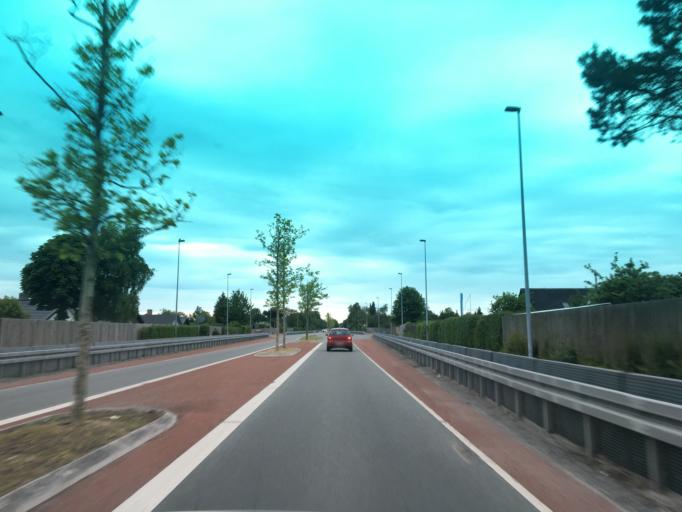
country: DK
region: Capital Region
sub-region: Albertslund Kommune
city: Albertslund
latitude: 55.6461
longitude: 12.3555
